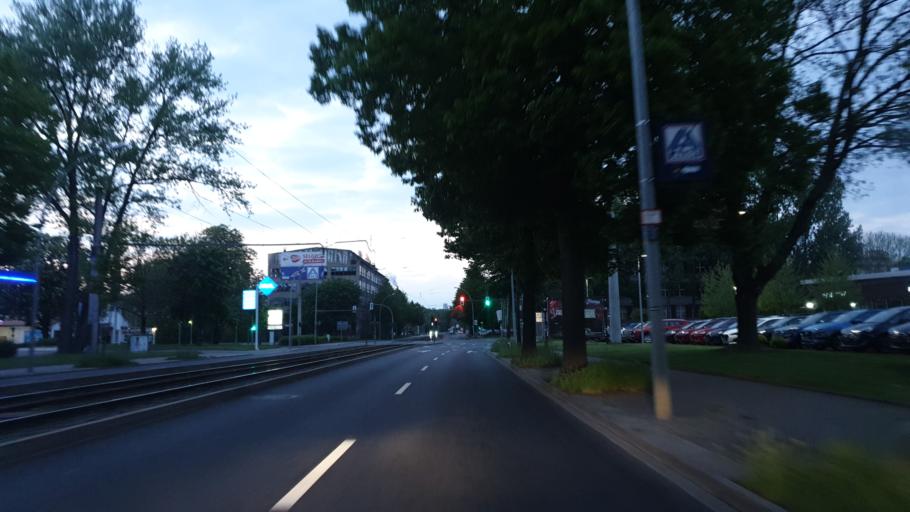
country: DE
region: Saxony
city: Chemnitz
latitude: 50.8138
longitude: 12.9130
